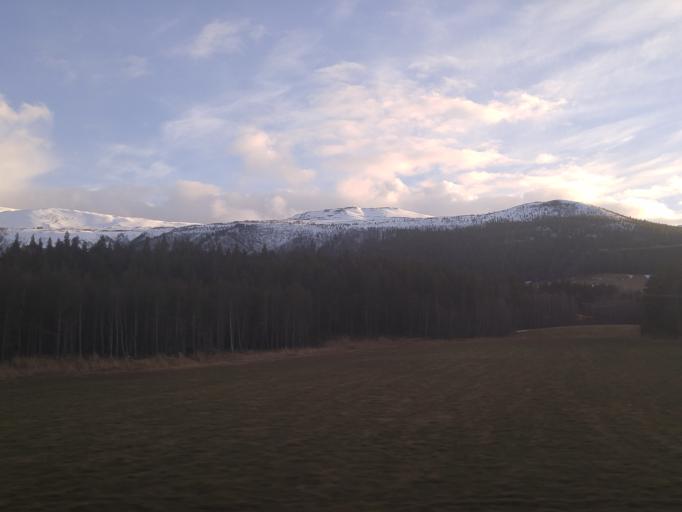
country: NO
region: Oppland
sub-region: Dovre
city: Dovre
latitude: 61.9518
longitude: 9.2756
